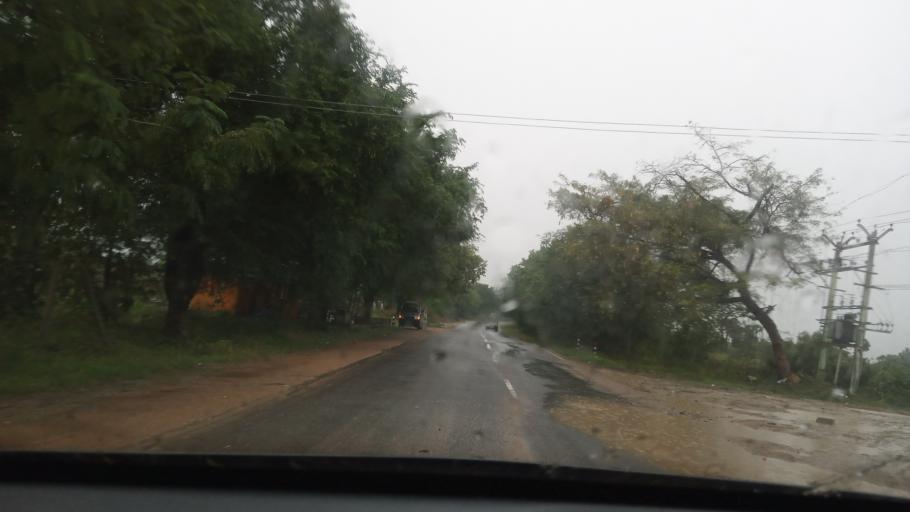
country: IN
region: Tamil Nadu
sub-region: Vellore
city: Kalavai
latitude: 12.8299
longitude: 79.4060
